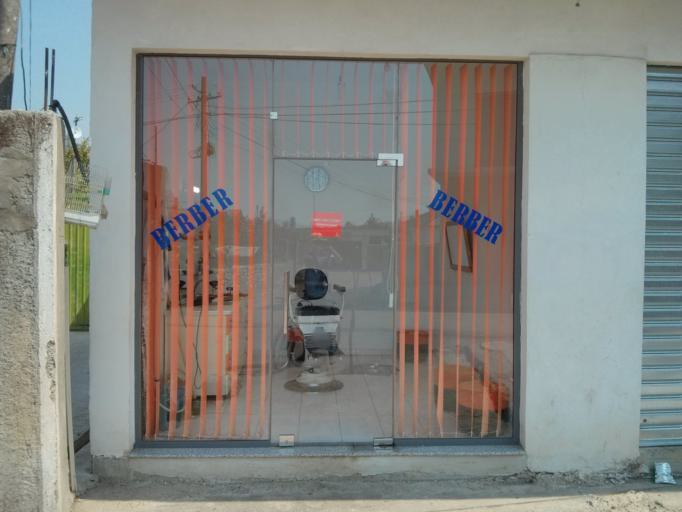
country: AL
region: Shkoder
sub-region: Rrethi i Malesia e Madhe
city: Gruemire
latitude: 42.1294
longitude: 19.5530
